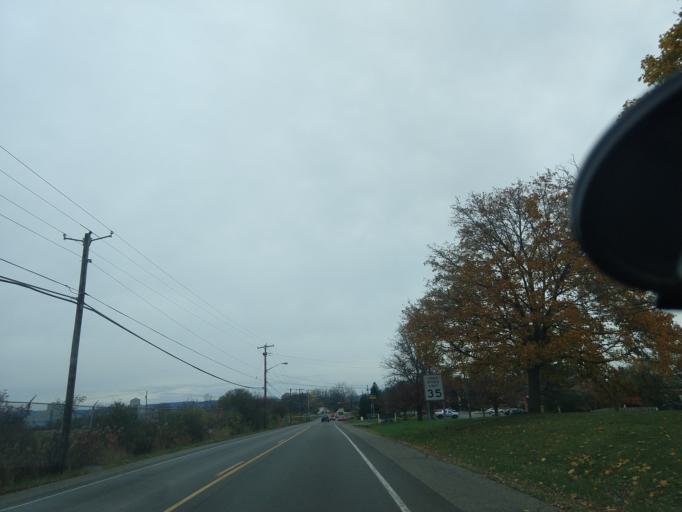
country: US
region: New York
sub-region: Tompkins County
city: East Ithaca
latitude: 42.4355
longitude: -76.4610
